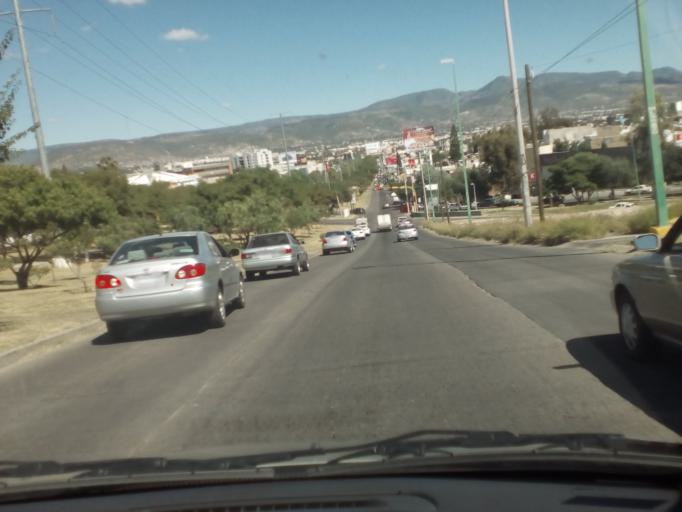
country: MX
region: Guanajuato
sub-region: Leon
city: La Ermita
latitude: 21.1499
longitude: -101.7045
